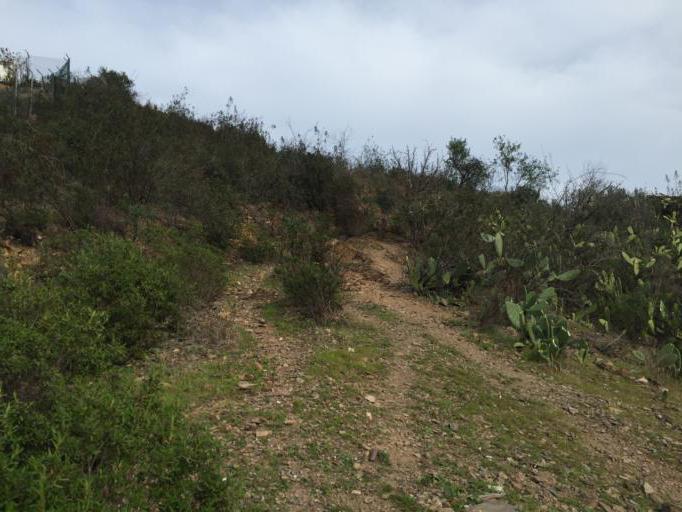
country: PT
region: Faro
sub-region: Tavira
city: Tavira
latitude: 37.2970
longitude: -7.6191
